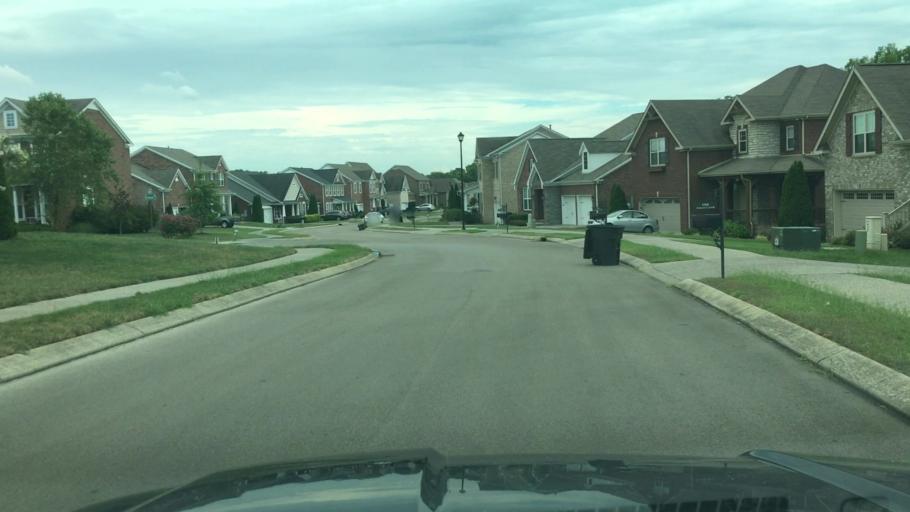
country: US
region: Tennessee
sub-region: Williamson County
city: Thompson's Station
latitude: 35.7606
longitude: -86.8750
